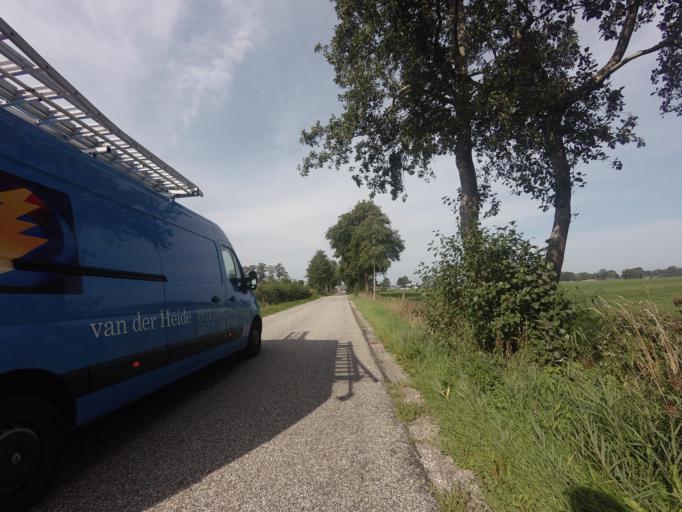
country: NL
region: Groningen
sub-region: Gemeente Leek
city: Leek
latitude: 53.1901
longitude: 6.3599
